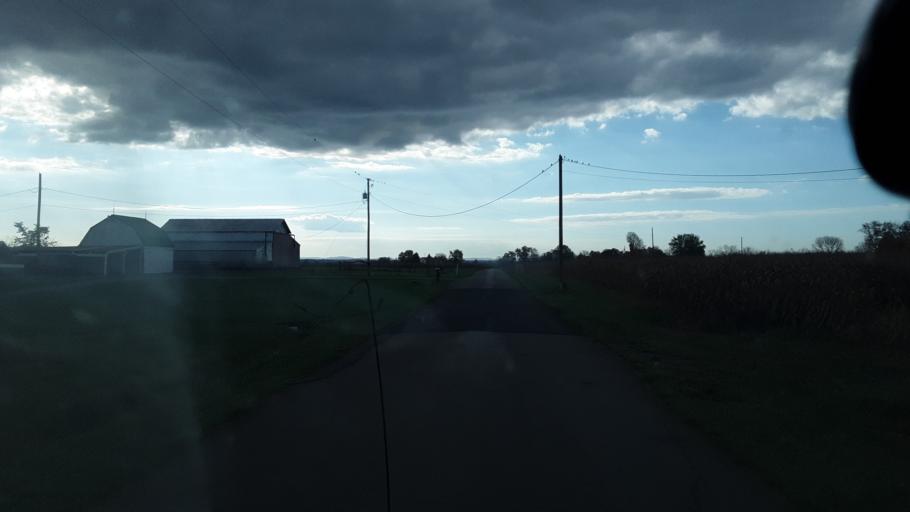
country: US
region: Ohio
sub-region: Highland County
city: Leesburg
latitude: 39.3619
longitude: -83.4803
